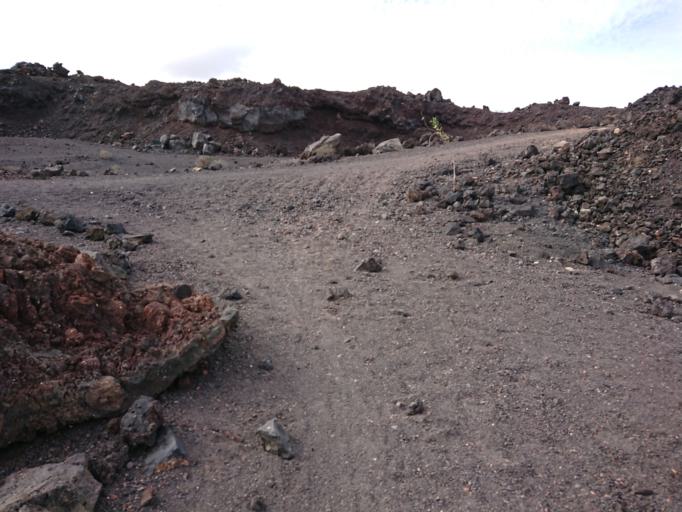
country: ES
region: Canary Islands
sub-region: Provincia de Las Palmas
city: Tinajo
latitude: 29.0104
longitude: -13.6778
